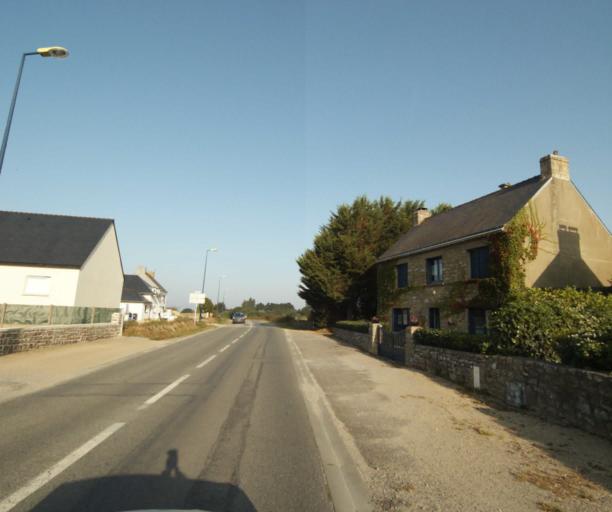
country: FR
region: Brittany
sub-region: Departement du Morbihan
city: Riantec
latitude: 47.7095
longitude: -3.2805
